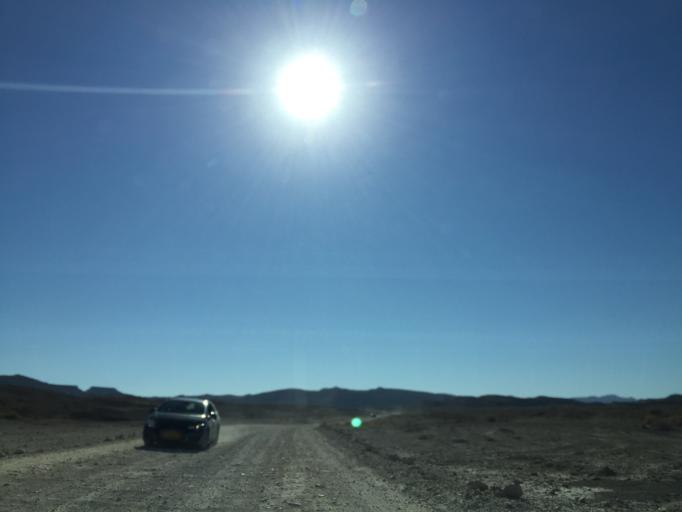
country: IL
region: Southern District
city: Mitzpe Ramon
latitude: 30.6116
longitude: 34.9023
